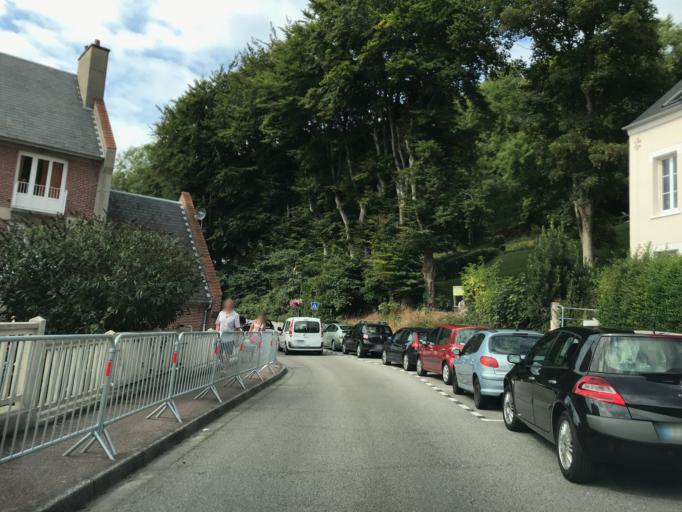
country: FR
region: Haute-Normandie
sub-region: Departement de la Seine-Maritime
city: Yport
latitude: 49.7369
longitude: 0.3172
